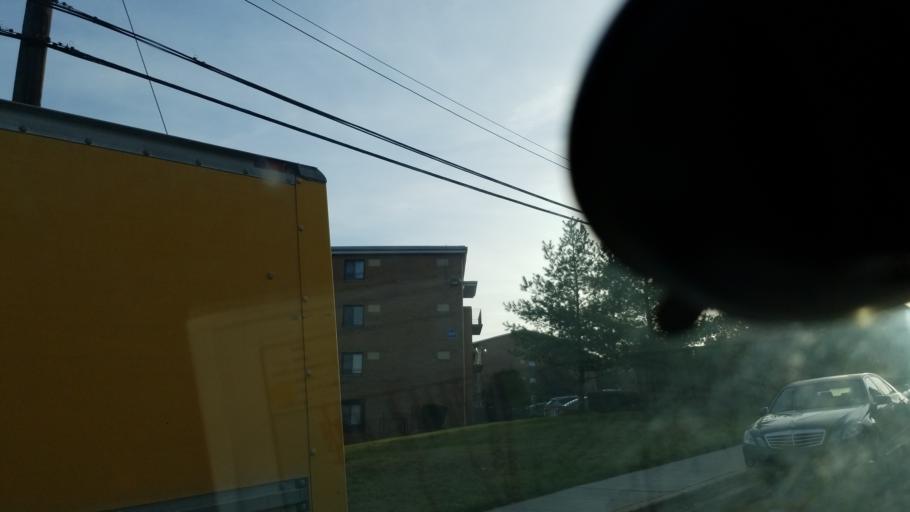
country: US
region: Maryland
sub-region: Prince George's County
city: Glassmanor
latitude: 38.8580
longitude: -76.9913
